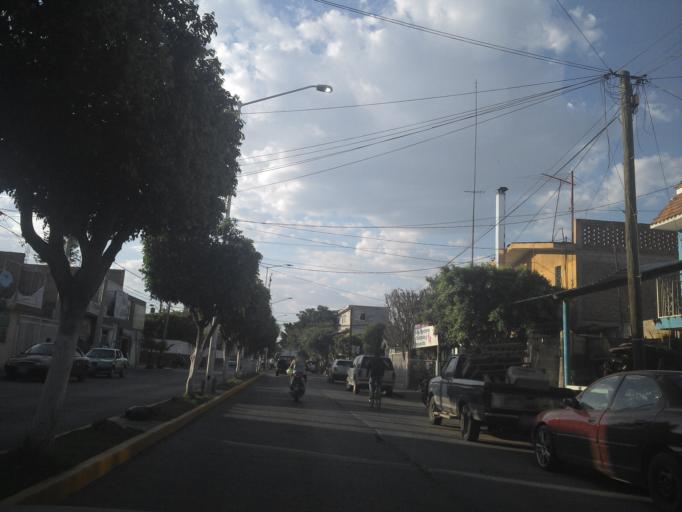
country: MX
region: Guanajuato
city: San Francisco del Rincon
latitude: 21.0240
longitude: -101.8625
